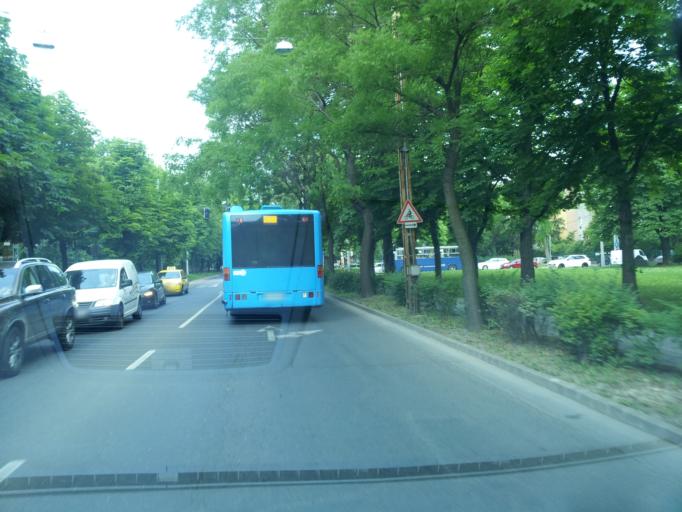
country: HU
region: Budapest
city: Budapest XII. keruelet
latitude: 47.5142
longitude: 19.0020
